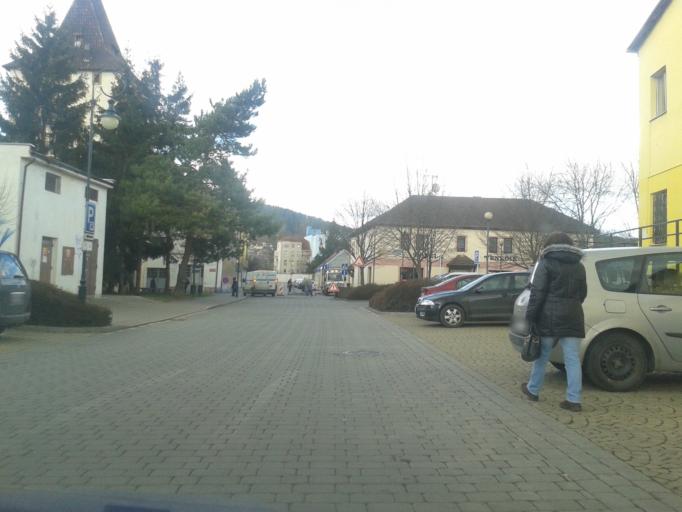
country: CZ
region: Central Bohemia
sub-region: Okres Beroun
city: Beroun
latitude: 49.9637
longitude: 14.0760
